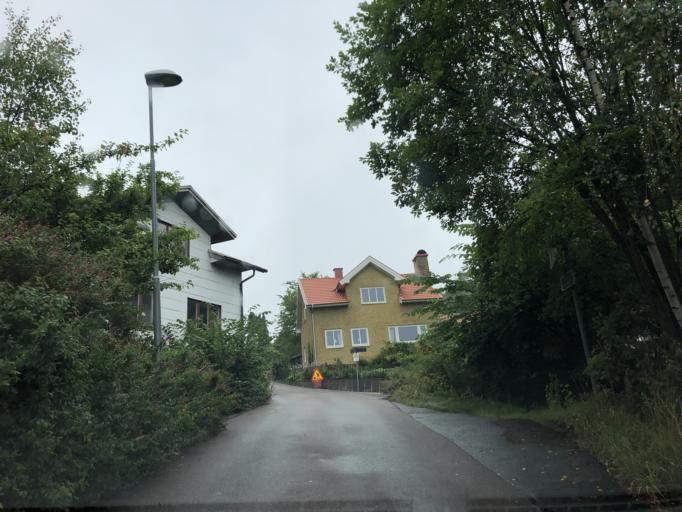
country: SE
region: Vaestra Goetaland
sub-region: Goteborg
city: Goeteborg
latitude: 57.7362
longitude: 11.9374
